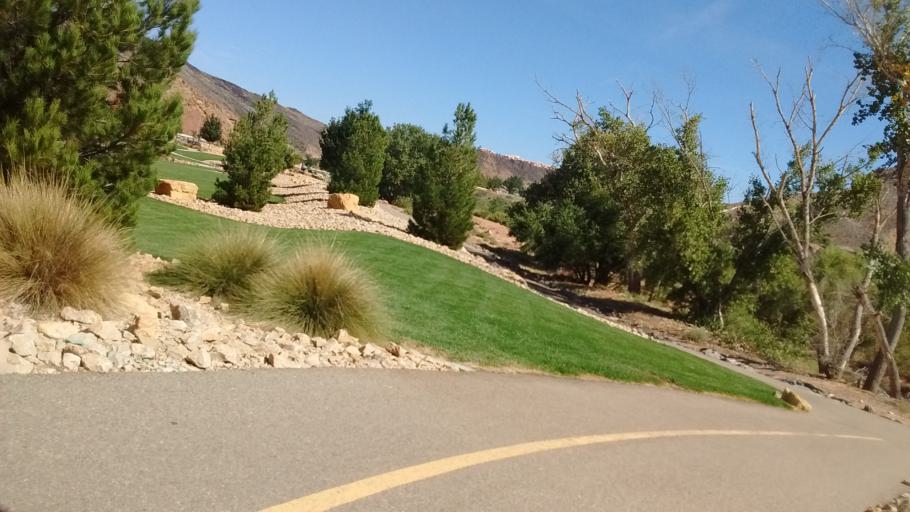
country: US
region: Utah
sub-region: Washington County
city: Washington
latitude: 37.1168
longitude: -113.5018
